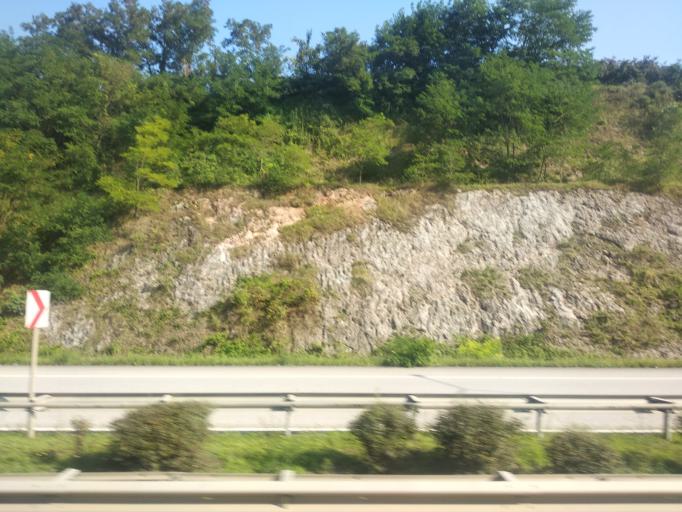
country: TR
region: Ordu
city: Ordu
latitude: 41.0114
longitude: 37.8333
